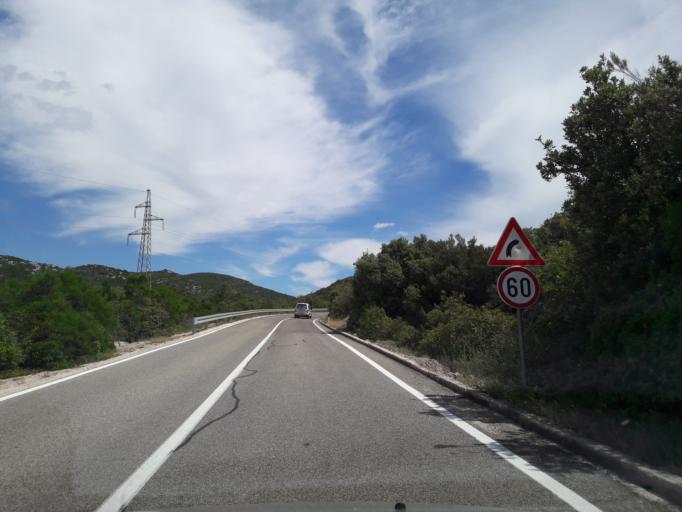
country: BA
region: Federation of Bosnia and Herzegovina
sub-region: Hercegovacko-Bosanski Kanton
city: Neum
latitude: 42.8966
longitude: 17.4933
